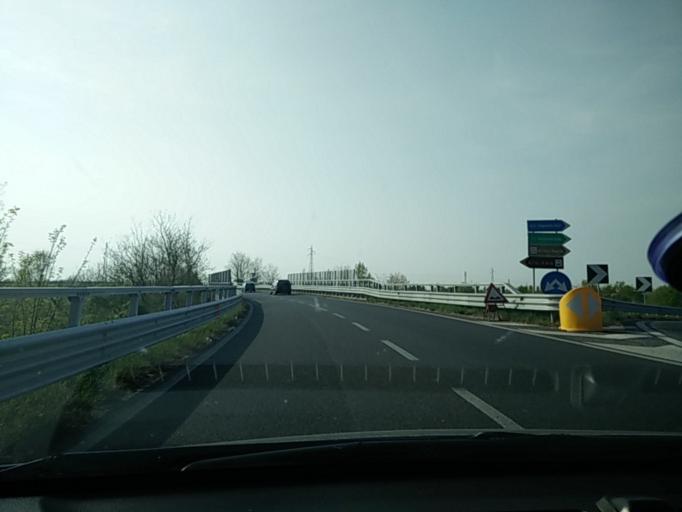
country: IT
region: Friuli Venezia Giulia
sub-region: Provincia di Udine
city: Pradamano
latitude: 46.0204
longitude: 13.2668
